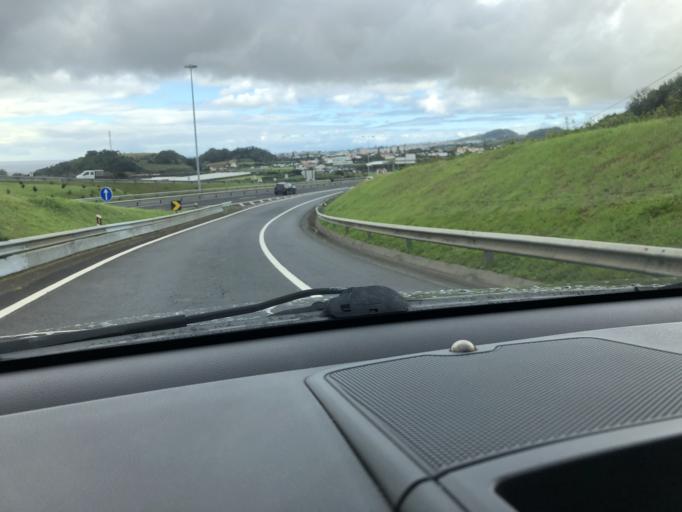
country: PT
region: Azores
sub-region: Ponta Delgada
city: Rosto de Cao
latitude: 37.7593
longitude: -25.6213
